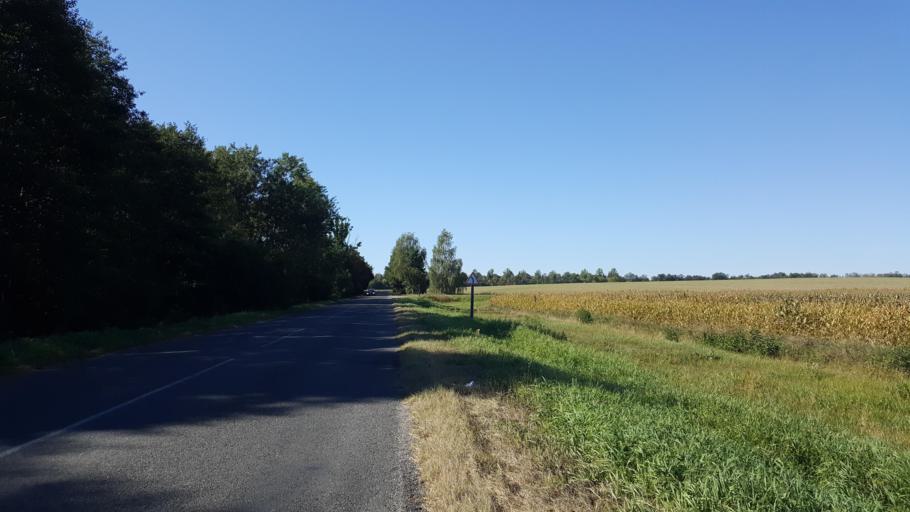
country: BY
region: Brest
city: Charnawchytsy
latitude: 52.3172
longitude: 23.6105
